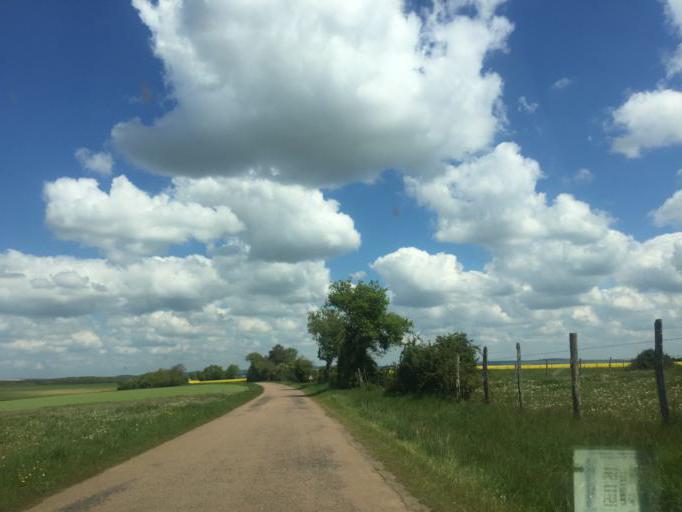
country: FR
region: Bourgogne
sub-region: Departement de l'Yonne
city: Fontenailles
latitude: 47.5073
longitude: 3.3435
